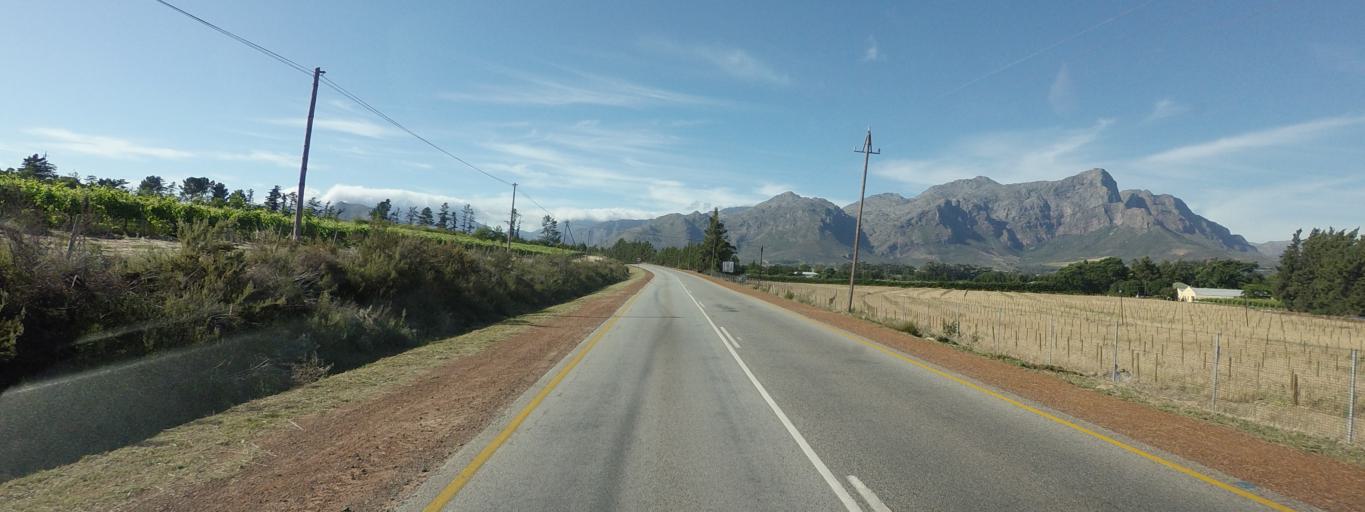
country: ZA
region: Western Cape
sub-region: Cape Winelands District Municipality
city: Paarl
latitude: -33.8605
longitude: 19.0393
